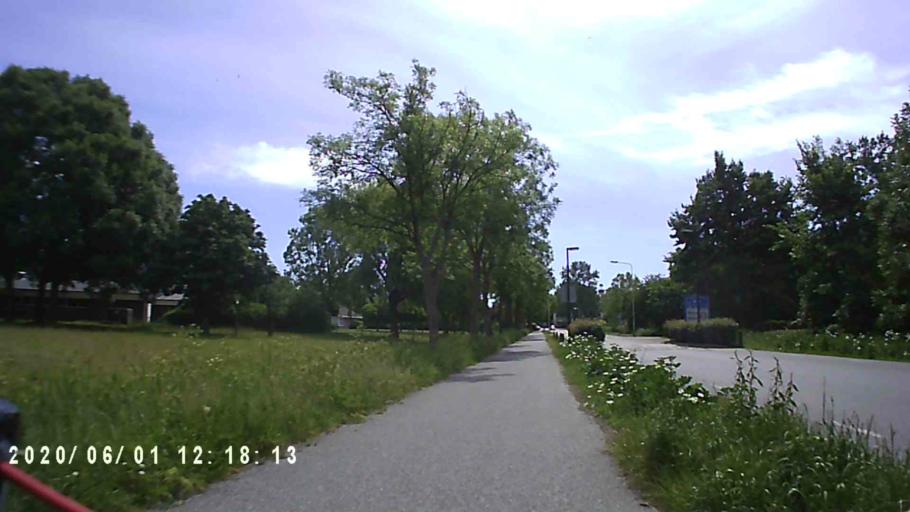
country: NL
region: Friesland
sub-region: Gemeente Harlingen
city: Harlingen
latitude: 53.1329
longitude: 5.4712
